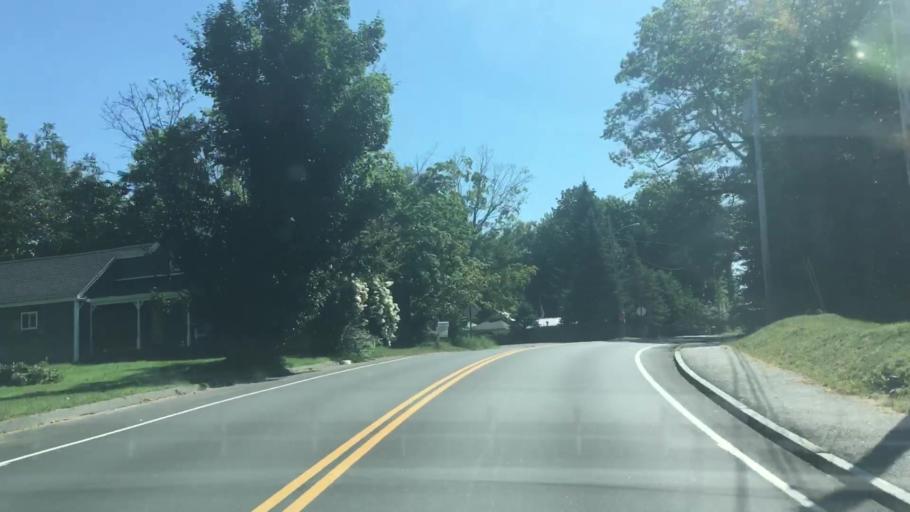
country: US
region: Maine
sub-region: Androscoggin County
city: Sabattus
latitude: 44.1187
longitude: -70.1053
